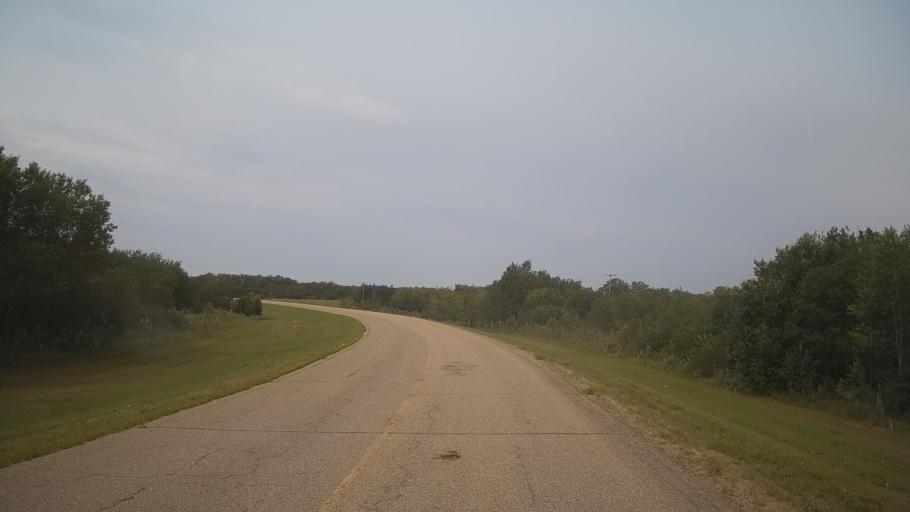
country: CA
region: Saskatchewan
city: Saskatoon
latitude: 51.8526
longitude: -106.5262
